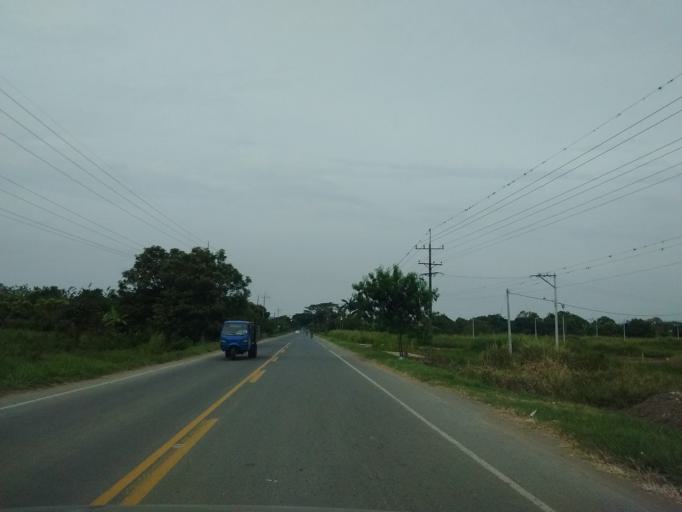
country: CO
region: Cauca
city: Puerto Tejada
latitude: 3.1843
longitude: -76.4506
